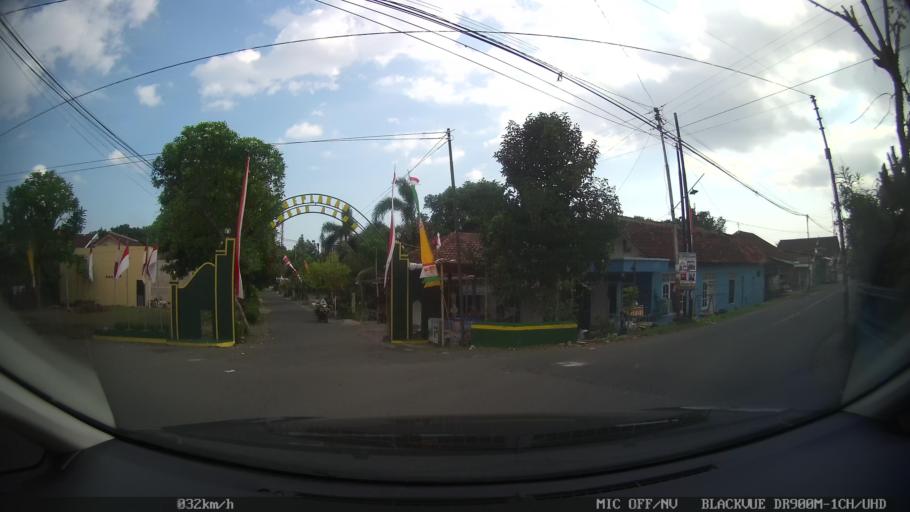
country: ID
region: Daerah Istimewa Yogyakarta
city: Gamping Lor
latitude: -7.7895
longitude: 110.3412
